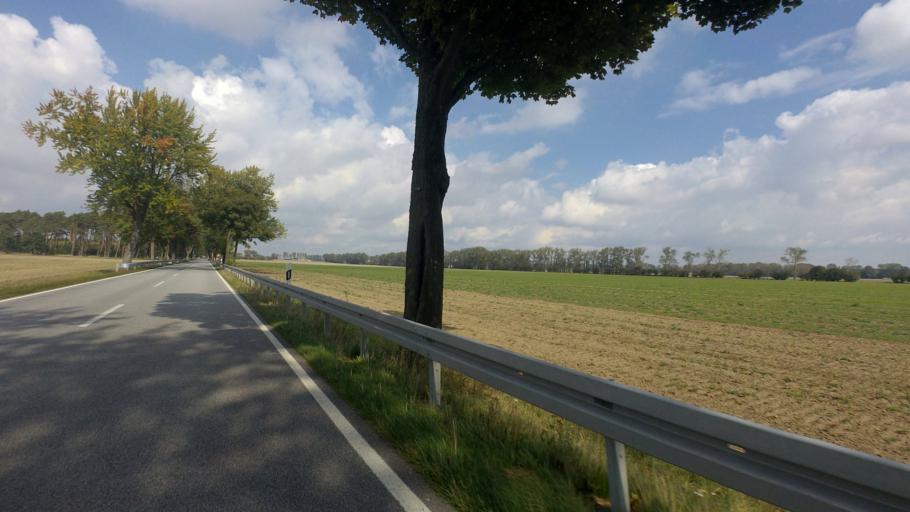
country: DE
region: Saxony-Anhalt
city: Holzdorf
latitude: 51.8893
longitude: 13.1418
